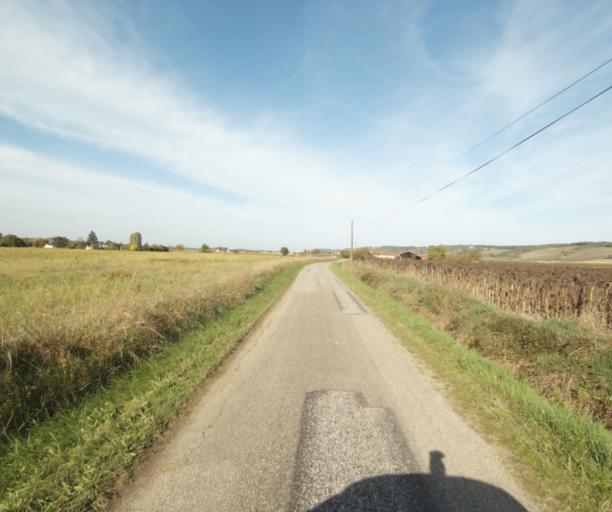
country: FR
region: Midi-Pyrenees
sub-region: Departement du Tarn-et-Garonne
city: Nohic
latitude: 43.9128
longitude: 1.4392
